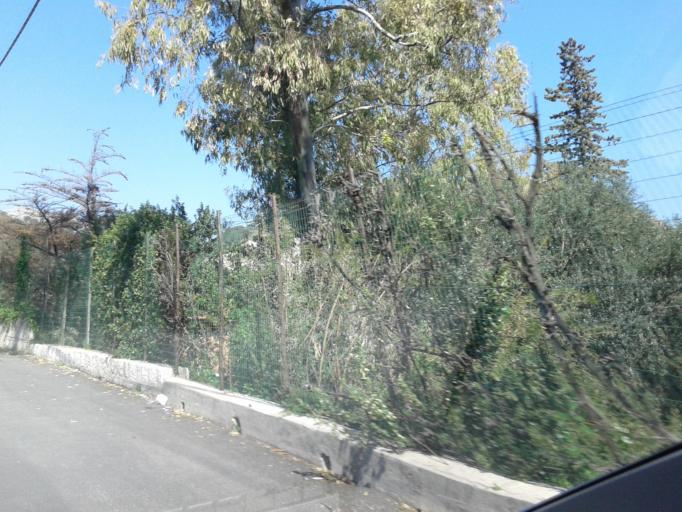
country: IT
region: Sicily
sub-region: Palermo
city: Piano dei Geli
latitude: 38.1152
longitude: 13.2939
